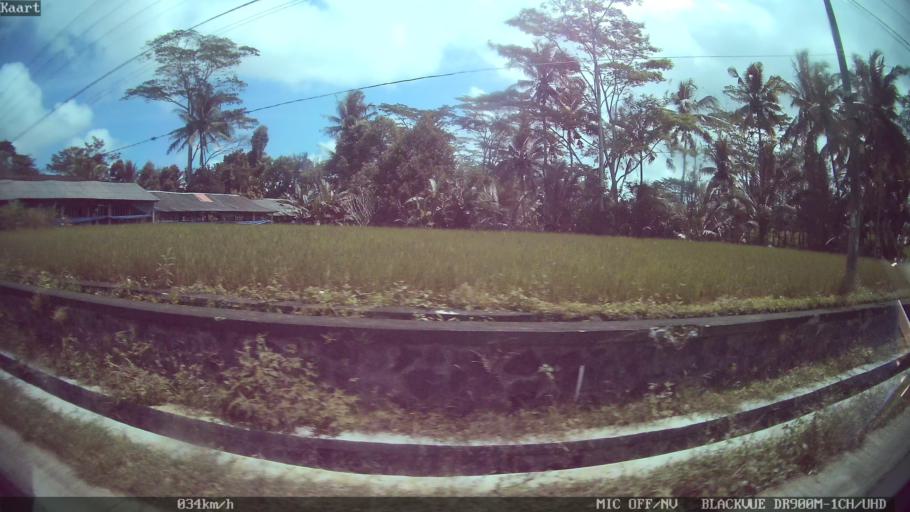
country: ID
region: Bali
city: Banjar Abuan
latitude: -8.4632
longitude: 115.3409
